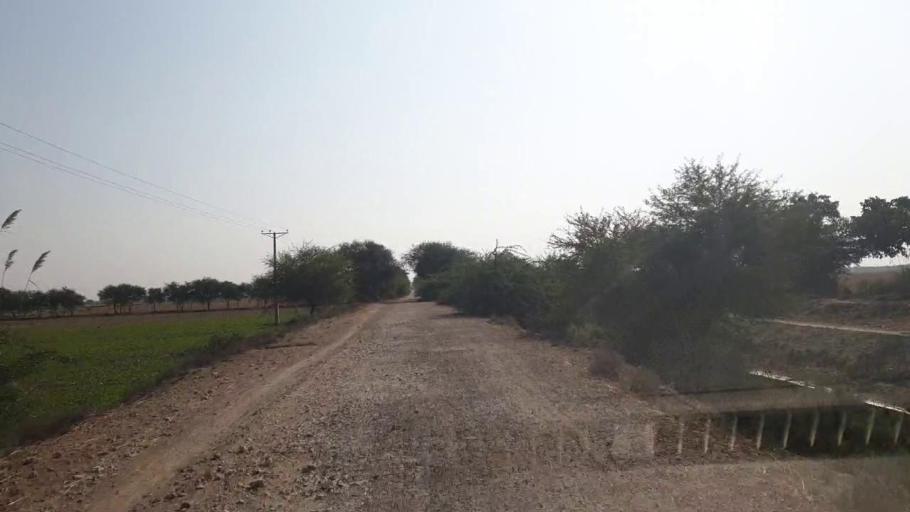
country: PK
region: Sindh
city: Kario
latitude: 24.9109
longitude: 68.6496
